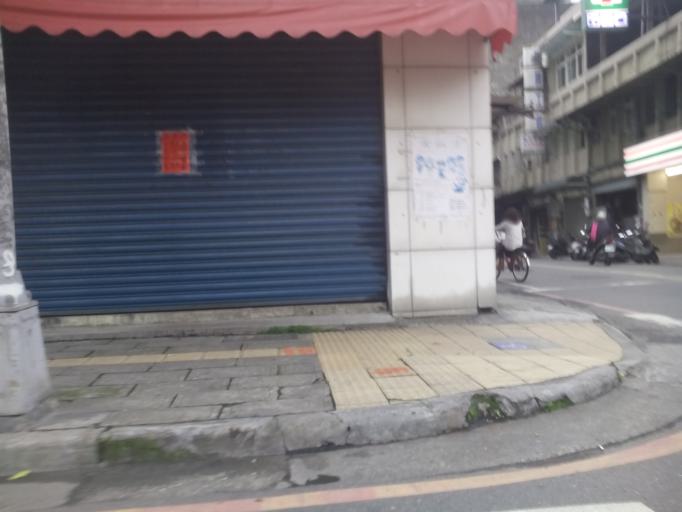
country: TW
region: Taipei
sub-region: Taipei
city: Banqiao
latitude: 24.9837
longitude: 121.4183
